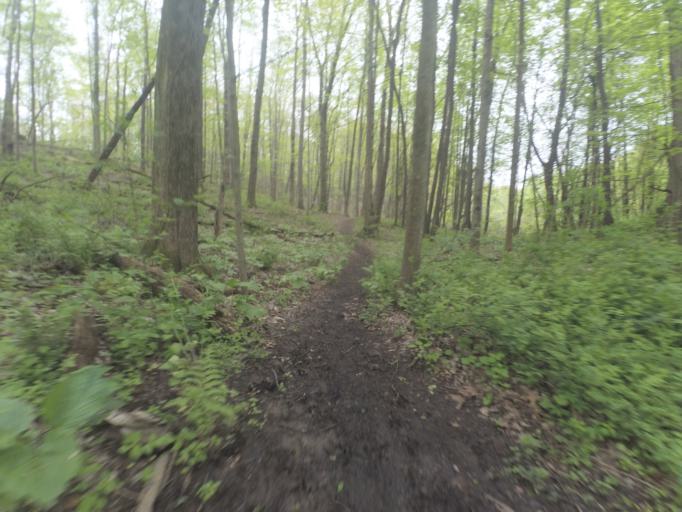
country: US
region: Ohio
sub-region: Portage County
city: Ravenna
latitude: 41.1742
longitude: -81.2992
